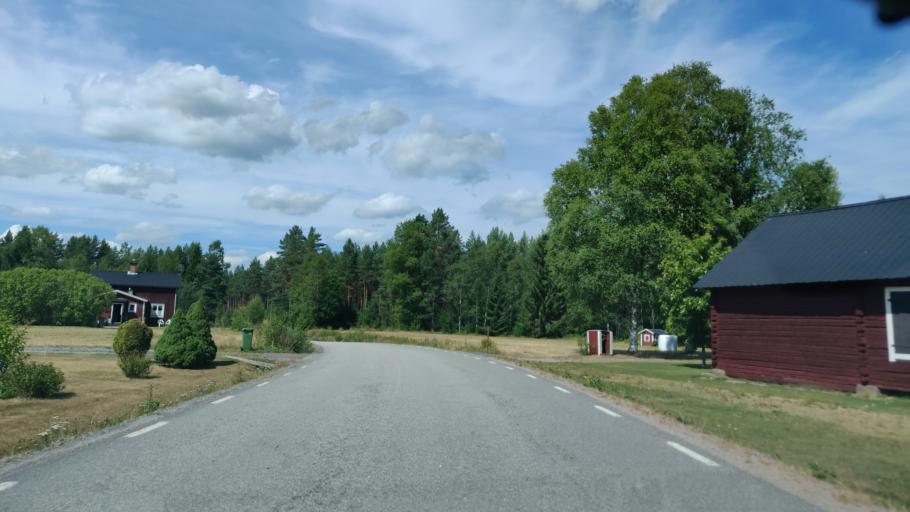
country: SE
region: Vaermland
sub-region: Hagfors Kommun
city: Ekshaerad
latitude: 60.0706
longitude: 13.5367
